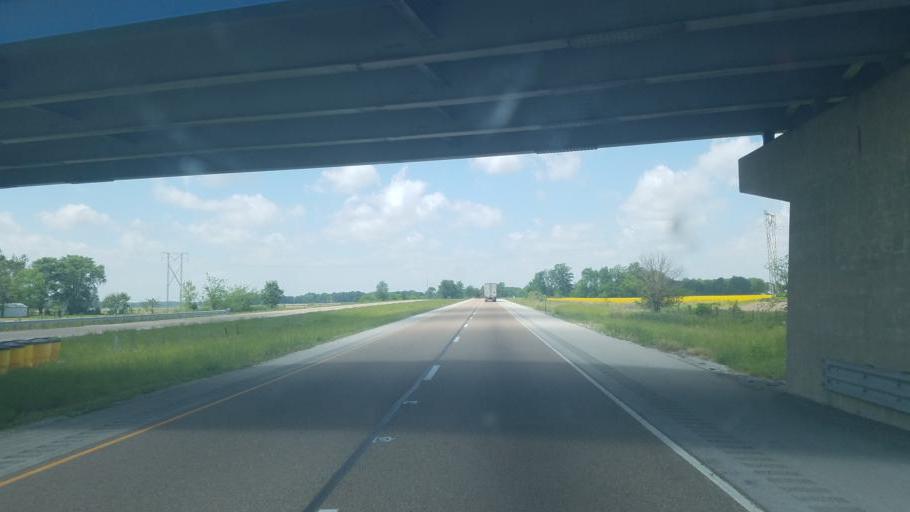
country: US
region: Illinois
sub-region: Cumberland County
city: Greenup
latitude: 39.2792
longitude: -88.0809
